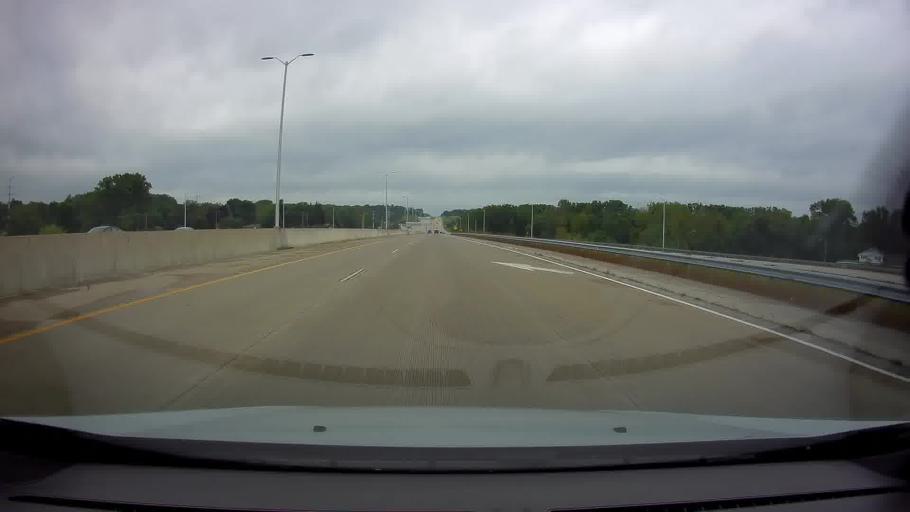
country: US
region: Wisconsin
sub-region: Brown County
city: Howard
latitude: 44.5436
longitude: -88.0896
